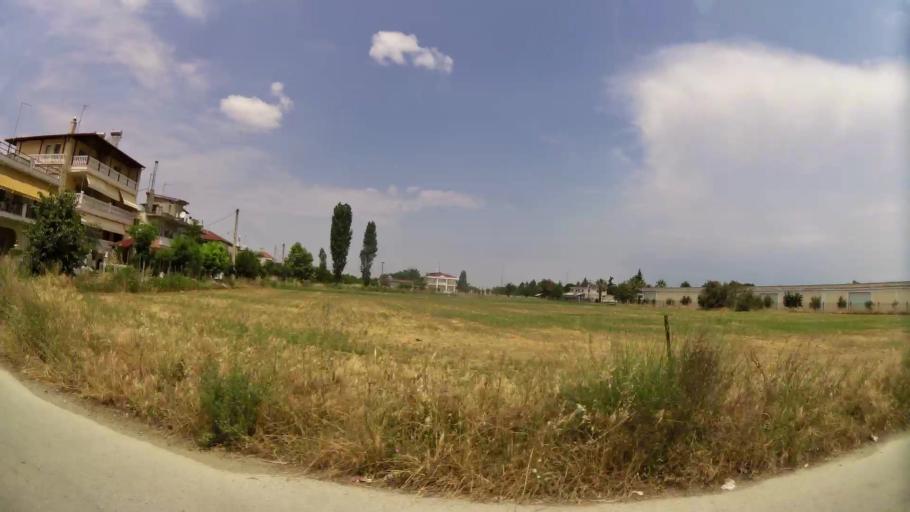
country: GR
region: Central Macedonia
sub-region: Nomos Pierias
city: Peristasi
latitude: 40.2721
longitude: 22.5464
